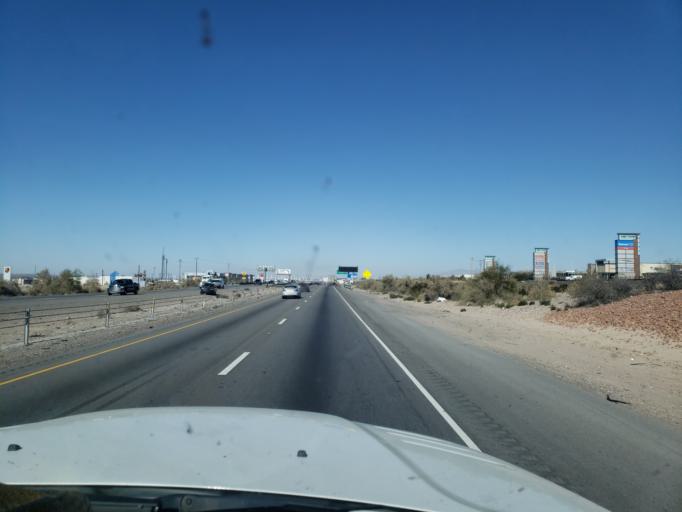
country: US
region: Texas
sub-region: El Paso County
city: Canutillo
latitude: 31.8836
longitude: -106.5820
